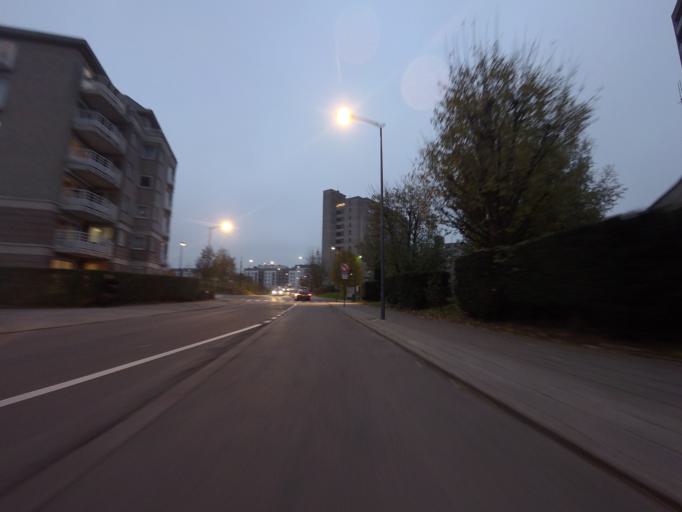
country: BE
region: Flanders
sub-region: Provincie Vlaams-Brabant
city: Diegem
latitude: 50.8543
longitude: 4.4254
